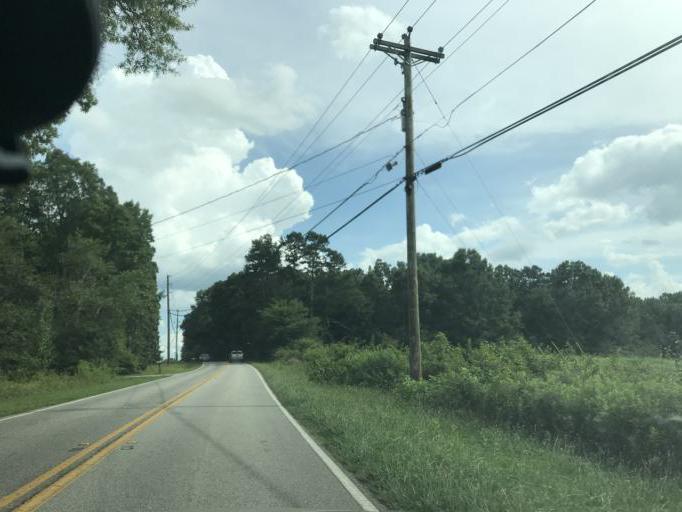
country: US
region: Georgia
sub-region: Forsyth County
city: Cumming
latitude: 34.2935
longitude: -84.1548
